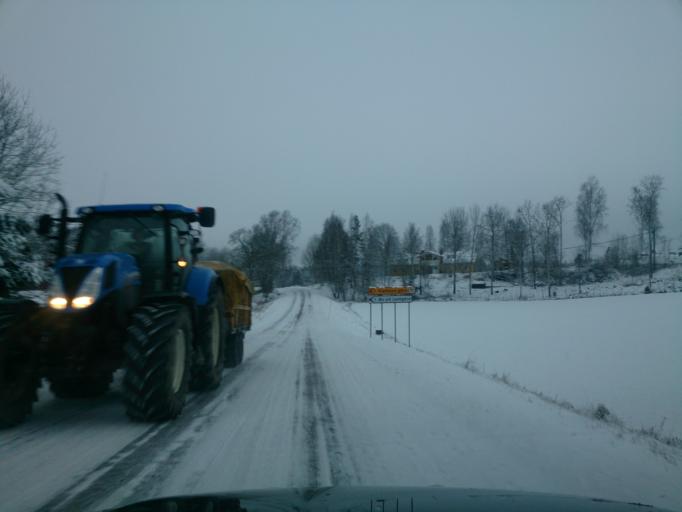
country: SE
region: OEstergoetland
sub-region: Norrkopings Kommun
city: Kimstad
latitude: 58.4203
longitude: 15.9141
